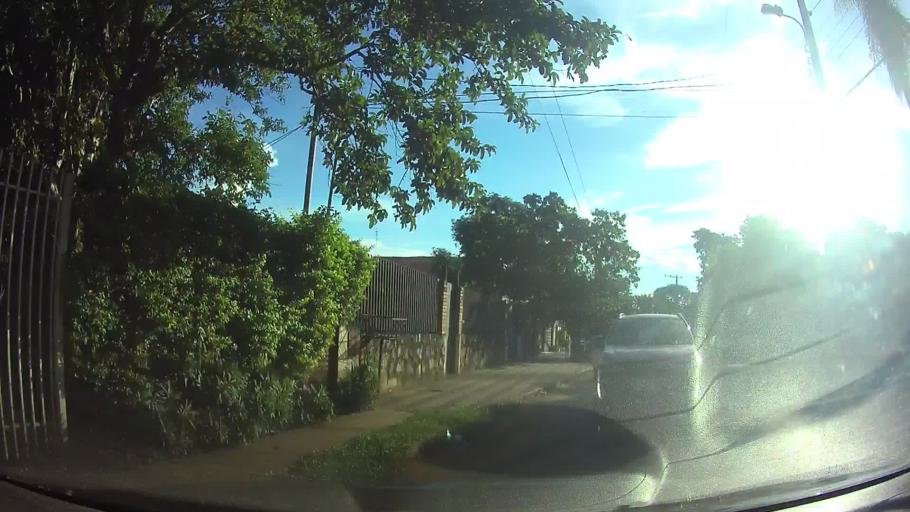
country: PY
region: Central
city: Villa Elisa
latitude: -25.3607
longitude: -57.5923
